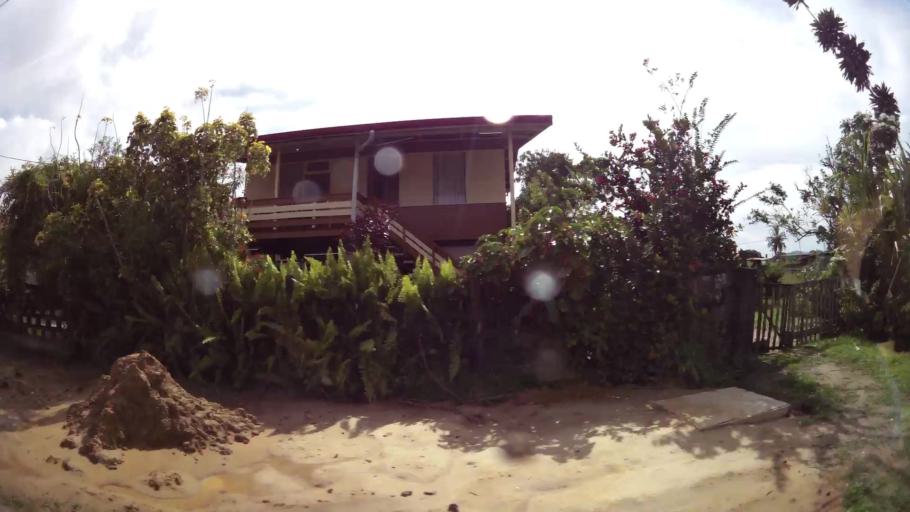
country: SR
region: Paramaribo
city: Paramaribo
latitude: 5.8443
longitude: -55.2065
